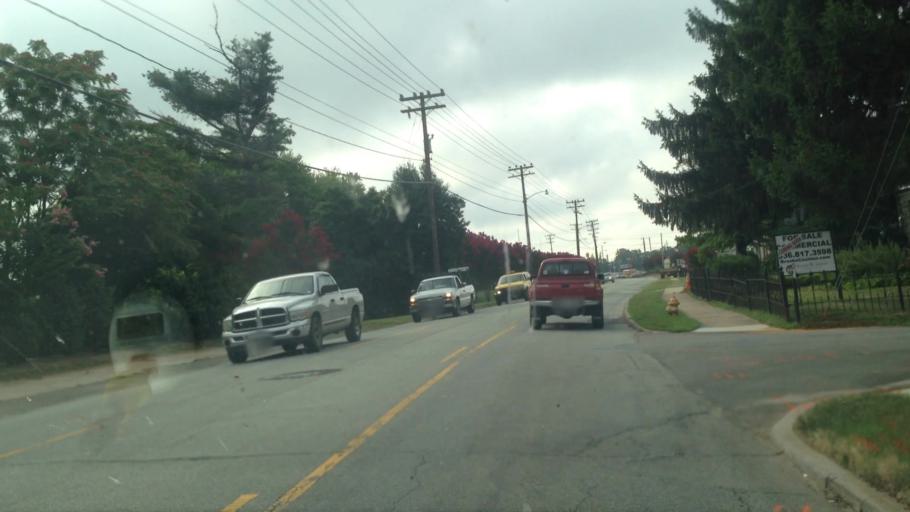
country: US
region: North Carolina
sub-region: Forsyth County
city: Kernersville
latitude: 36.1179
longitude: -80.0684
